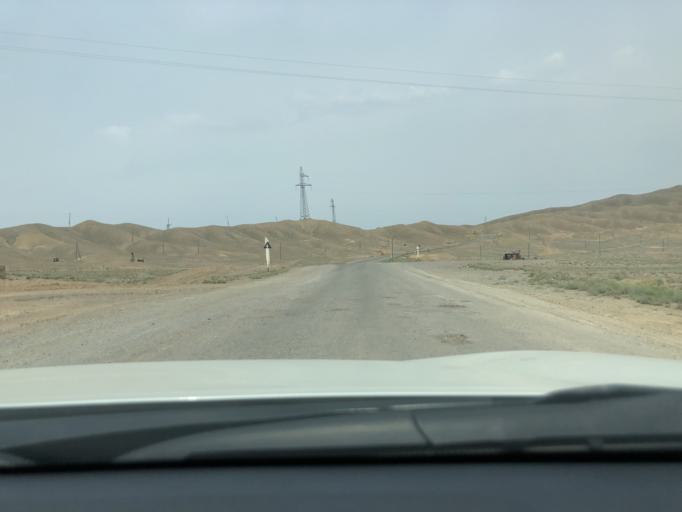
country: TJ
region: Viloyati Sughd
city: Kim
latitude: 40.2142
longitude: 70.4751
